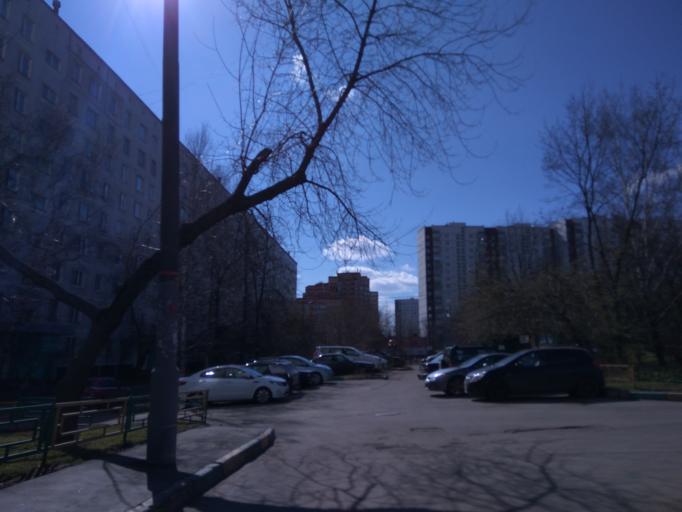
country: RU
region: Moscow
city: Ivanovskoye
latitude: 55.7793
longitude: 37.8330
